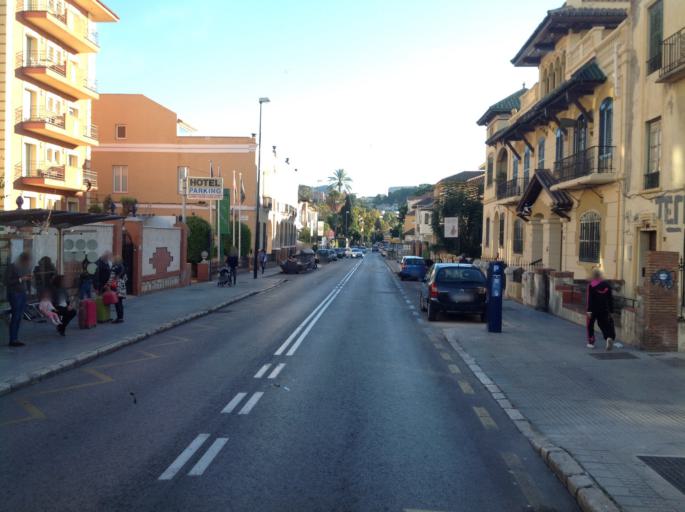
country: ES
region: Andalusia
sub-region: Provincia de Malaga
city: Malaga
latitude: 36.7217
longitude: -4.4016
